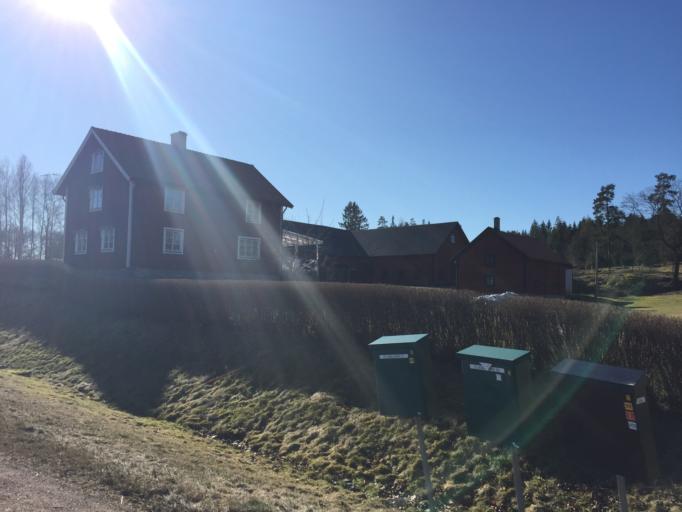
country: SE
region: OEstergoetland
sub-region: Finspangs Kommun
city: Finspang
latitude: 58.7850
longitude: 15.7693
